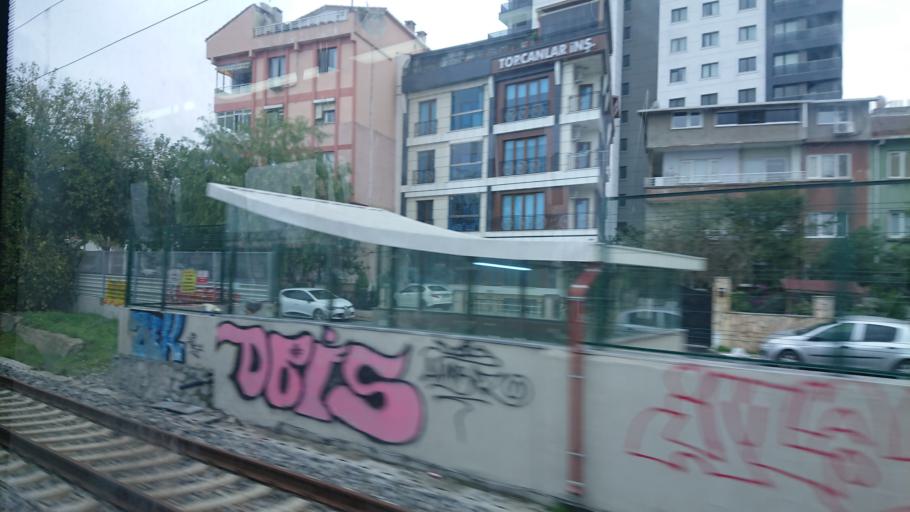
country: TR
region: Istanbul
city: Mahmutbey
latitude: 41.0009
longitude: 28.7685
